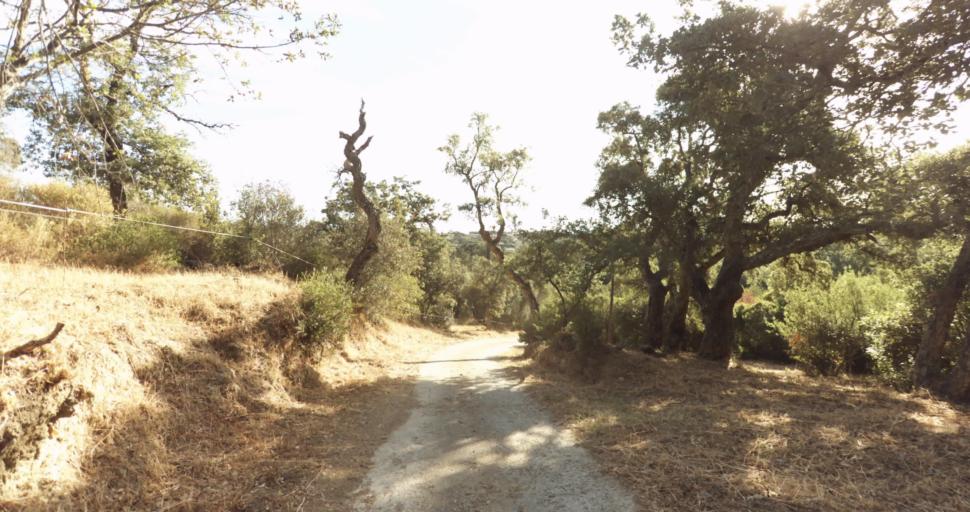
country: FR
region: Provence-Alpes-Cote d'Azur
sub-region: Departement du Var
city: Saint-Tropez
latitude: 43.2570
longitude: 6.6266
